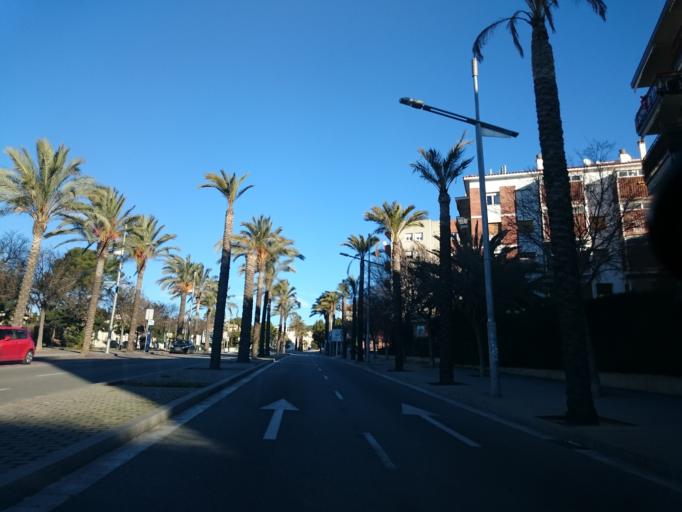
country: ES
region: Catalonia
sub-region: Provincia de Barcelona
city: Sitges
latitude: 41.2404
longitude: 1.8063
